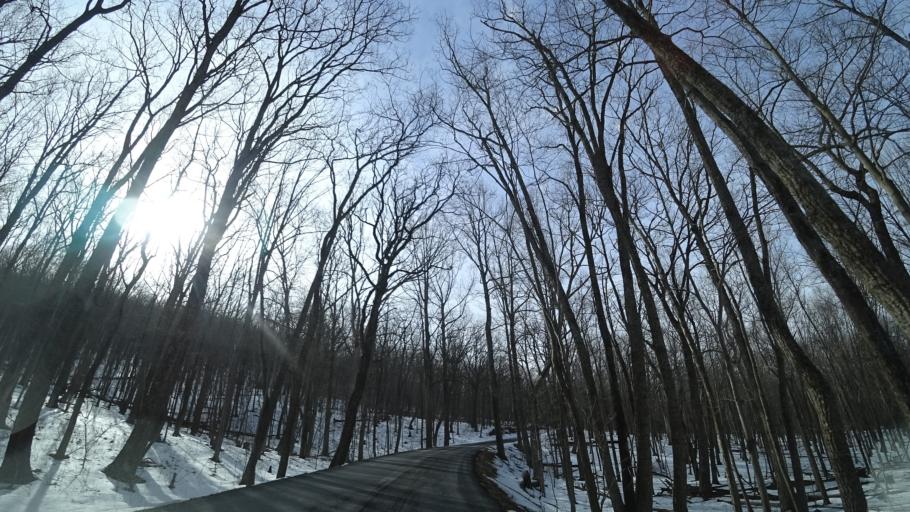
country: US
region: Virginia
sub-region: Shenandoah County
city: Basye
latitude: 38.9305
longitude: -78.6894
